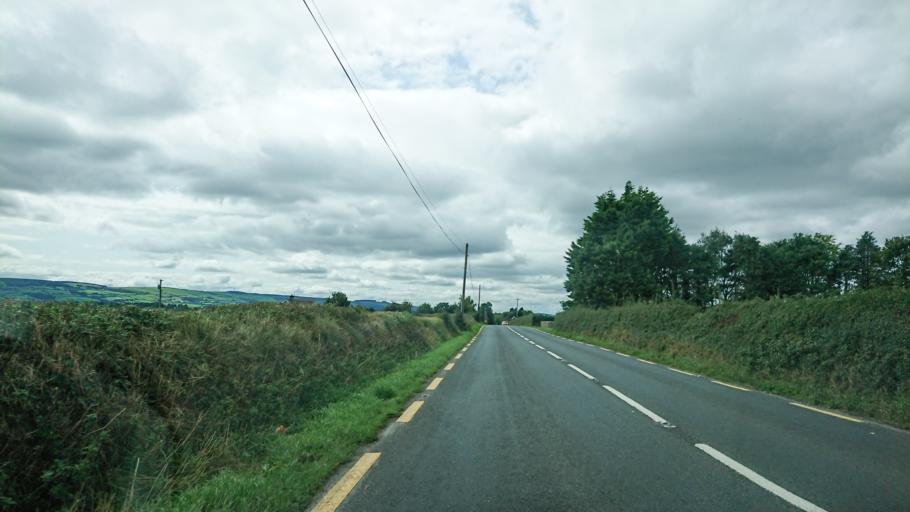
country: IE
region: Munster
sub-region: Waterford
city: Dungarvan
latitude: 52.1092
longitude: -7.6312
